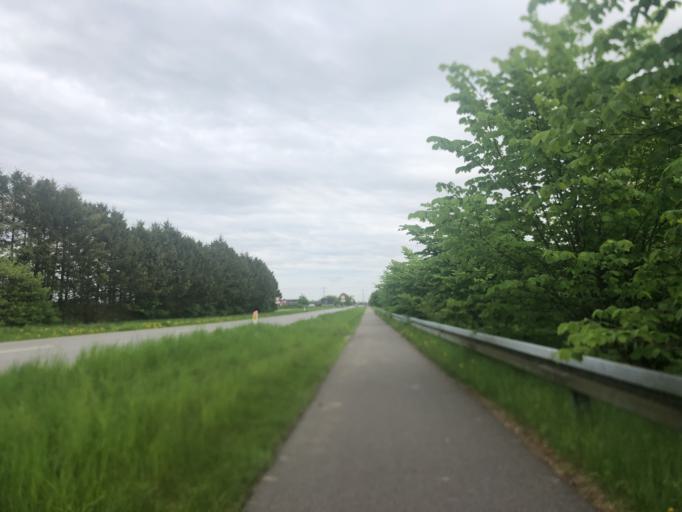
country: DK
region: Zealand
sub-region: Ringsted Kommune
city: Ringsted
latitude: 55.4490
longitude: 11.8643
